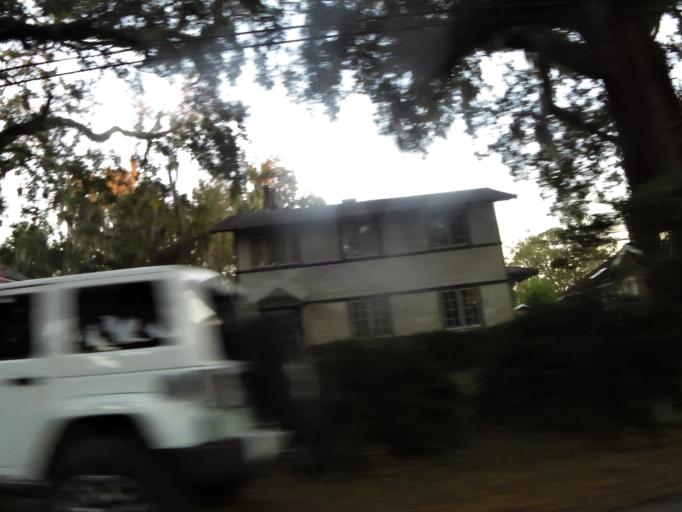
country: US
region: Florida
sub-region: Duval County
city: Jacksonville
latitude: 30.2945
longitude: -81.7035
